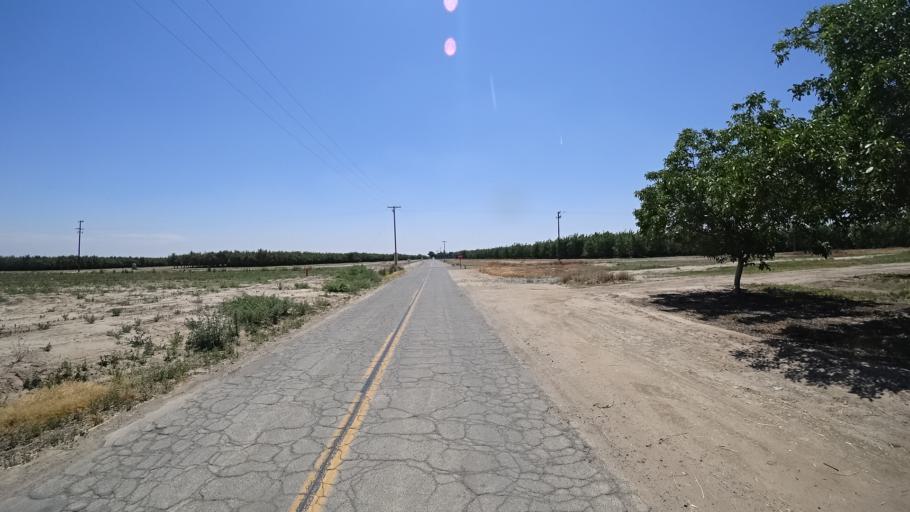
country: US
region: California
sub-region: Kings County
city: Lucerne
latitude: 36.4165
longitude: -119.6010
